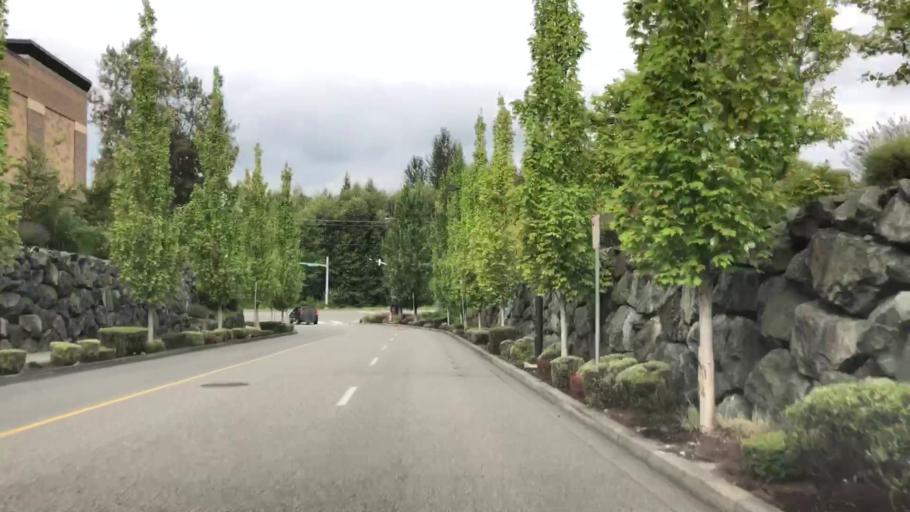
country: US
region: Washington
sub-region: Snohomish County
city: Fobes Hill
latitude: 47.9440
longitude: -122.1081
